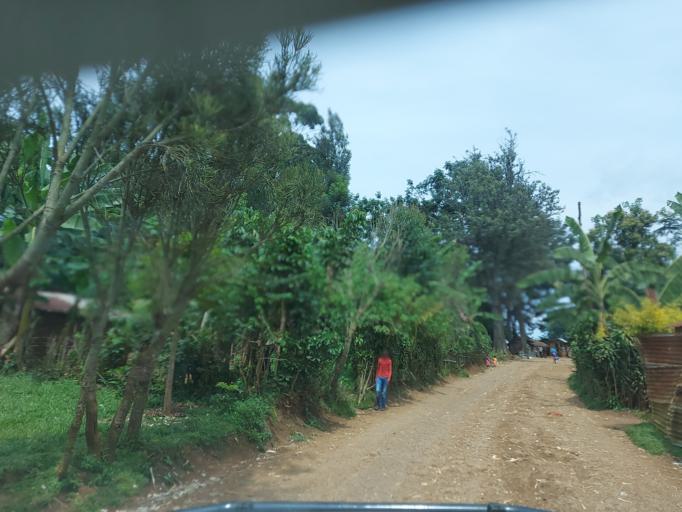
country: RW
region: Western Province
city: Cyangugu
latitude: -2.2341
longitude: 28.8530
